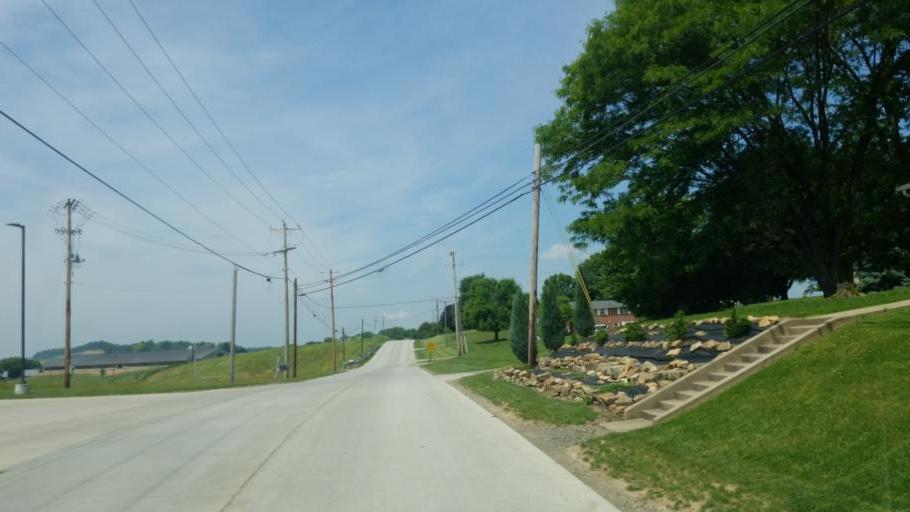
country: US
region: Ohio
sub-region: Tuscarawas County
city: Sugarcreek
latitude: 40.5178
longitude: -81.6799
